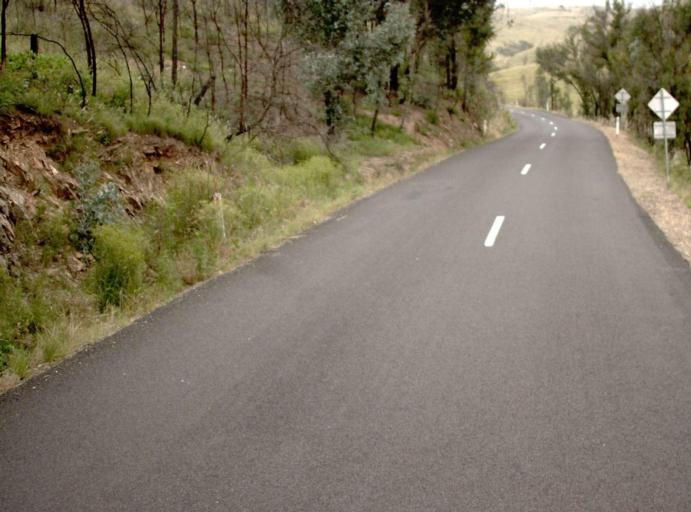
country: AU
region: Victoria
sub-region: Wellington
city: Heyfield
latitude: -37.8507
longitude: 146.7075
